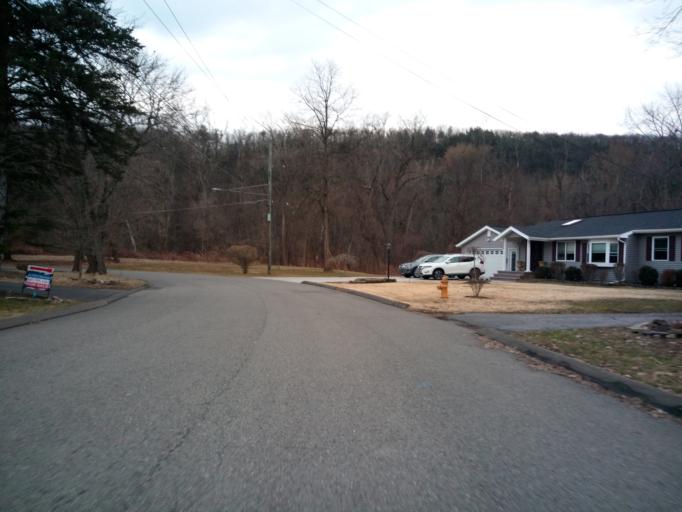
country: US
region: New York
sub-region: Chemung County
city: West Elmira
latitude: 42.0771
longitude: -76.8553
